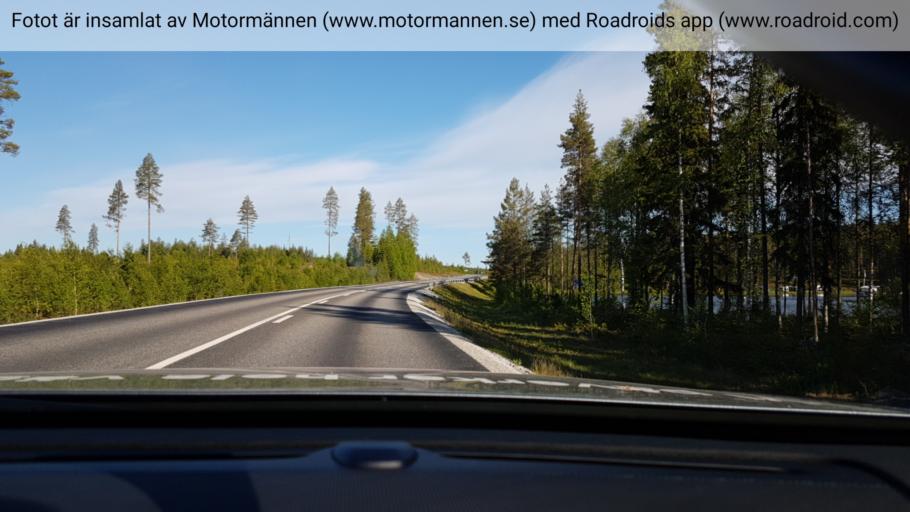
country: SE
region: Vaesterbotten
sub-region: Vindelns Kommun
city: Vindeln
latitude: 64.0554
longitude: 19.6523
